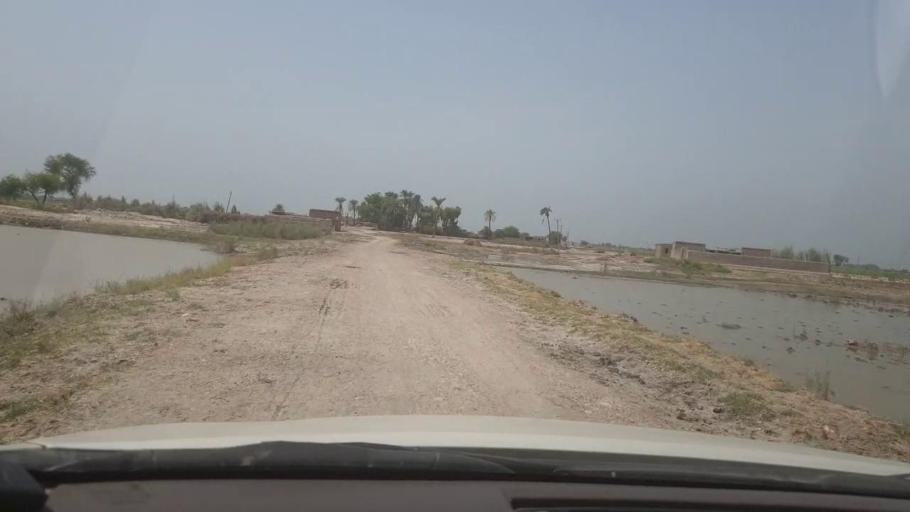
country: PK
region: Sindh
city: Shikarpur
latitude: 27.9609
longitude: 68.5914
